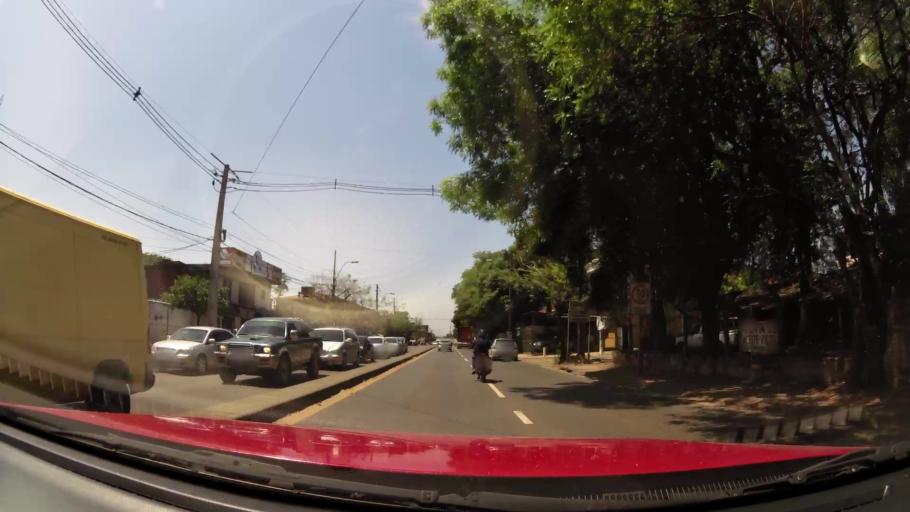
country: PY
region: Central
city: Fernando de la Mora
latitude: -25.3231
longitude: -57.5641
